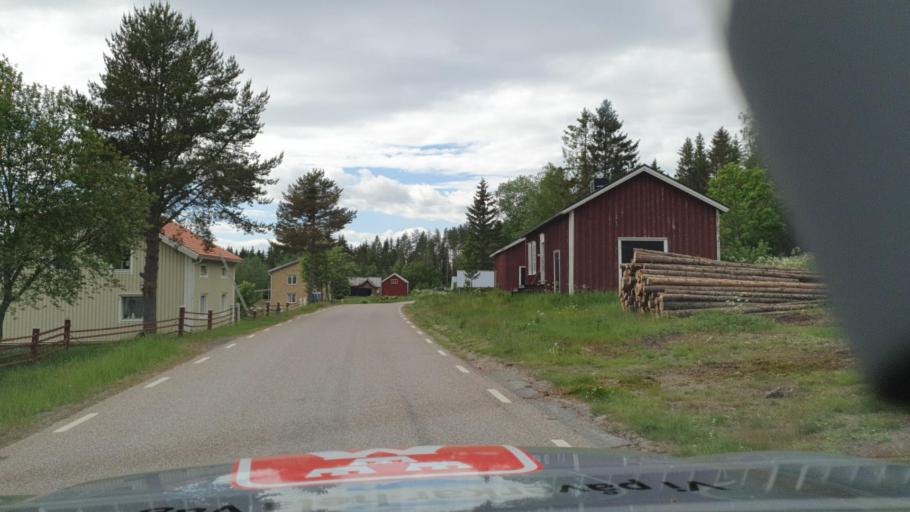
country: SE
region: Vaesternorrland
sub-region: Kramfors Kommun
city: Nordingra
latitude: 62.8621
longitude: 18.3349
